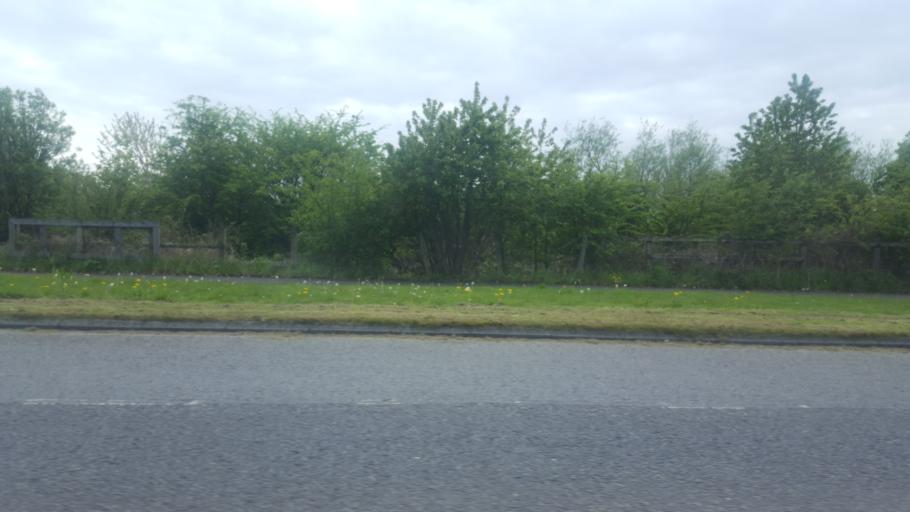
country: GB
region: Scotland
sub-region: Falkirk
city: Polmont
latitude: 56.0009
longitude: -3.7060
